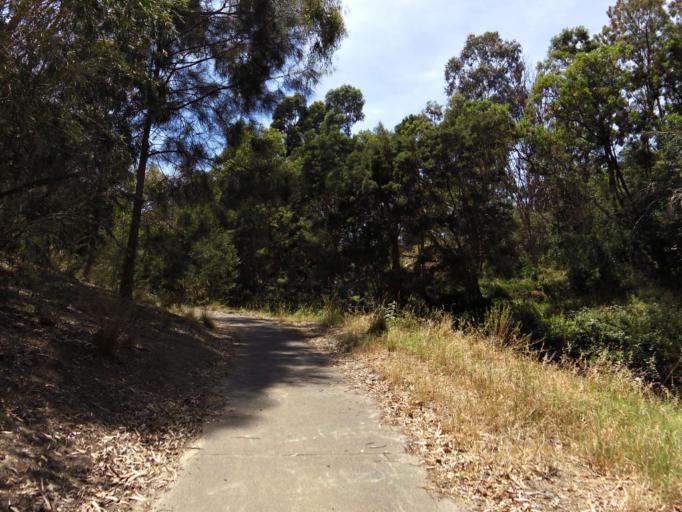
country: AU
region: Victoria
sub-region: Boroondara
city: Camberwell
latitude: -37.8496
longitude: 145.0719
